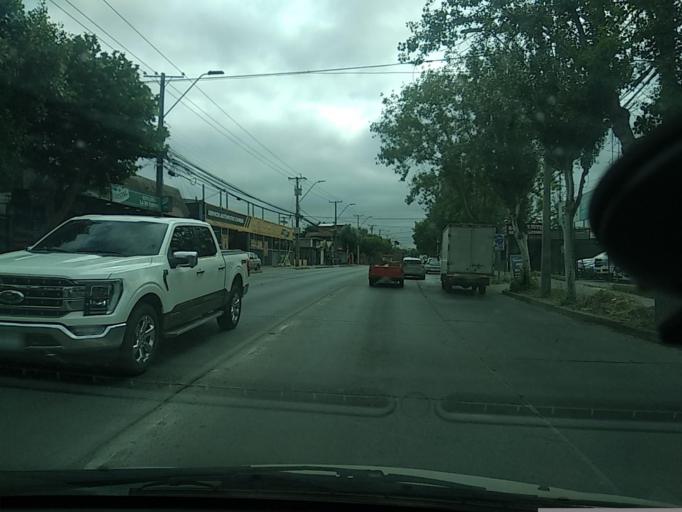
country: CL
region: Valparaiso
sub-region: Provincia de Marga Marga
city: Villa Alemana
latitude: -33.0453
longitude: -71.3895
